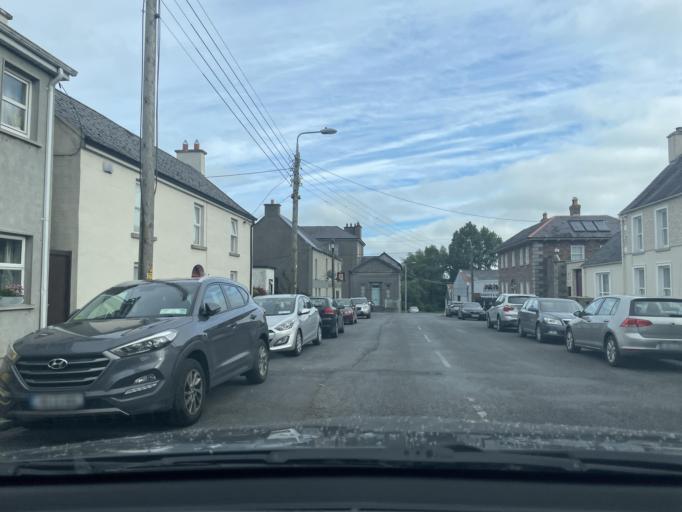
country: IE
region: Leinster
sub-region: County Carlow
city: Bagenalstown
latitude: 52.7021
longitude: -6.9618
